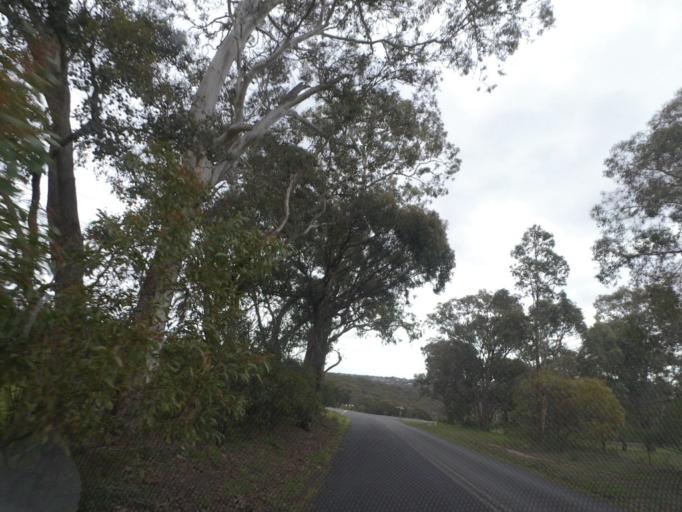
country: AU
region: Victoria
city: Plenty
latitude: -37.6679
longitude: 145.1036
